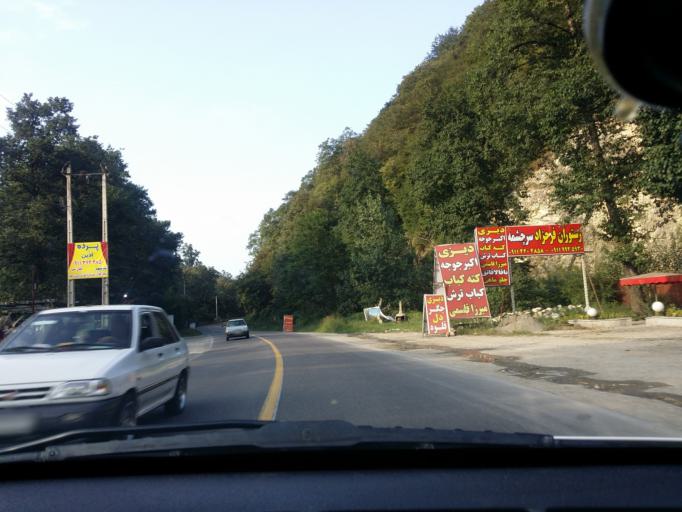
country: IR
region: Mazandaran
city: Chalus
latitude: 36.6065
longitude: 51.3864
